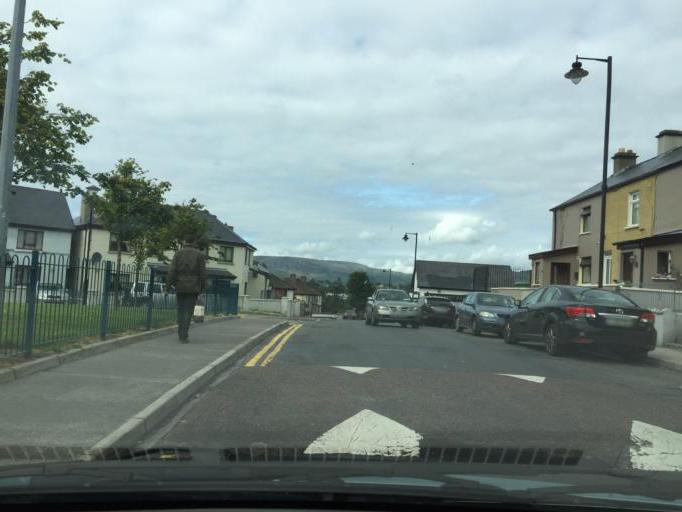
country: IE
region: Connaught
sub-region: Sligo
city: Sligo
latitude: 54.2753
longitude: -8.4729
